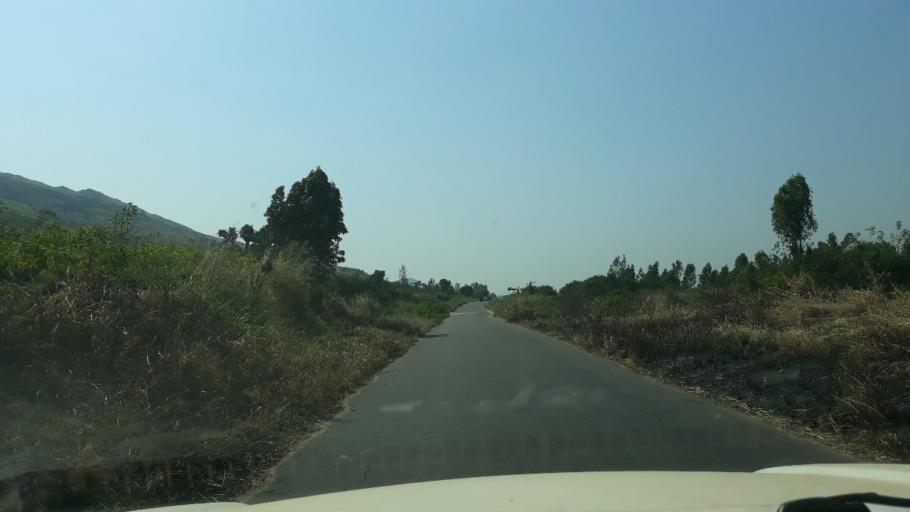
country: CD
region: South Kivu
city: Uvira
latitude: -3.2613
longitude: 29.1614
